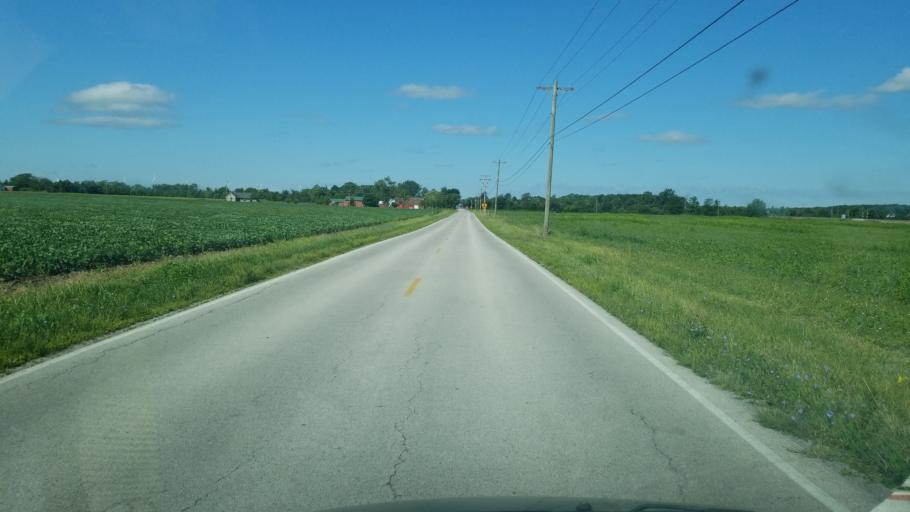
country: US
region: Ohio
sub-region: Hancock County
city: Findlay
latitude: 41.1092
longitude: -83.5873
